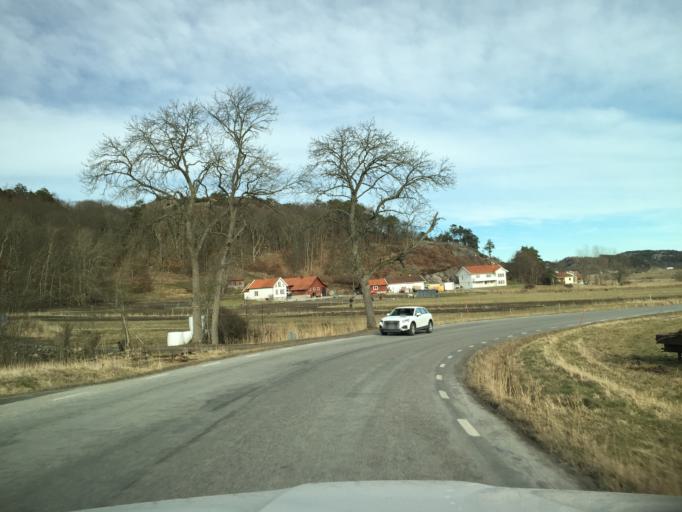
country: SE
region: Vaestra Goetaland
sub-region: Tjorns Kommun
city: Skaerhamn
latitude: 58.0373
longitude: 11.5802
